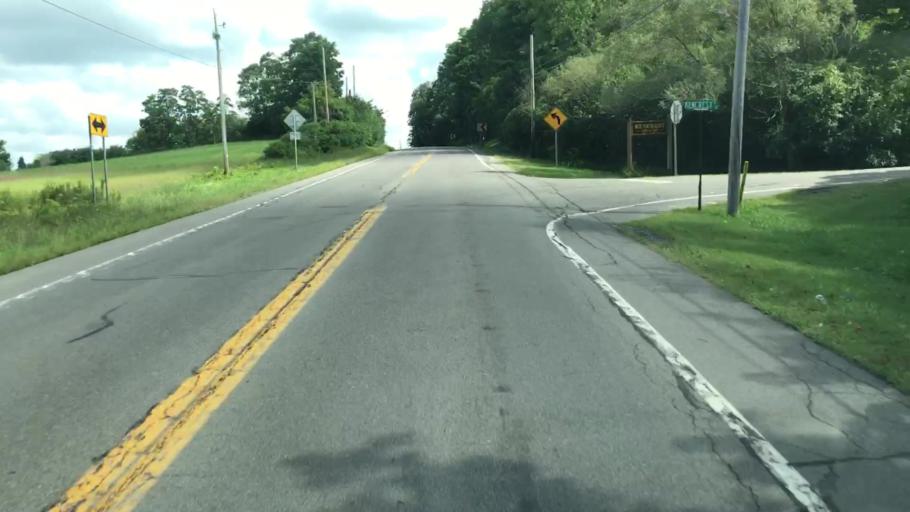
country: US
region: New York
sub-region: Onondaga County
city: Marcellus
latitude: 42.9835
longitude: -76.2814
